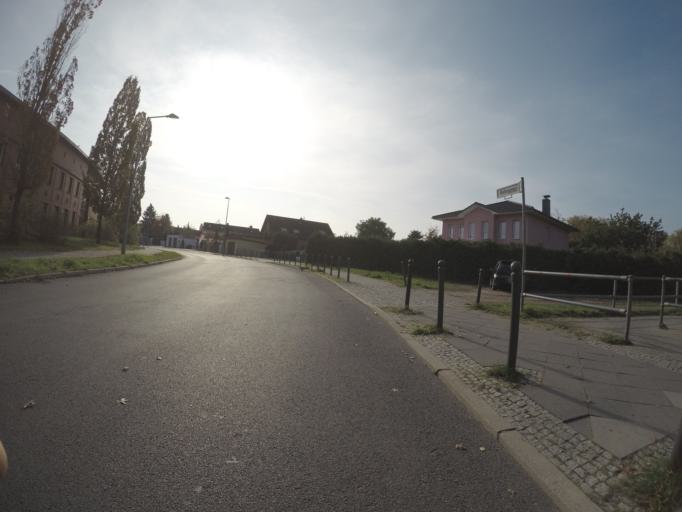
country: DE
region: Berlin
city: Altglienicke
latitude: 52.4026
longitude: 13.5383
